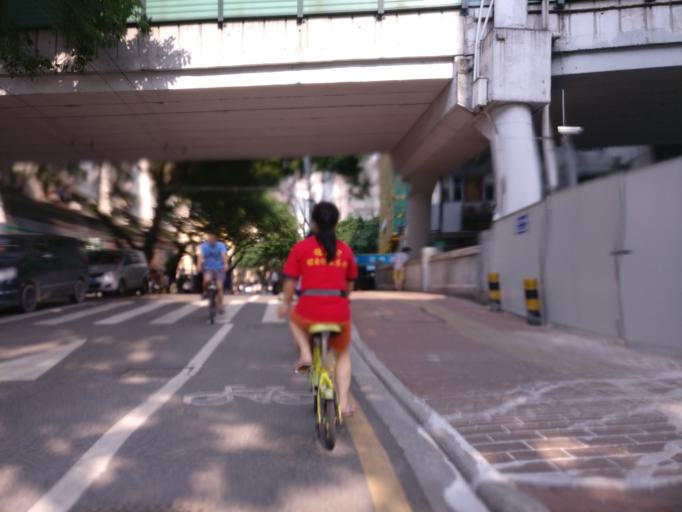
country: CN
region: Guangdong
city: Guangzhou
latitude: 23.1252
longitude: 113.2730
